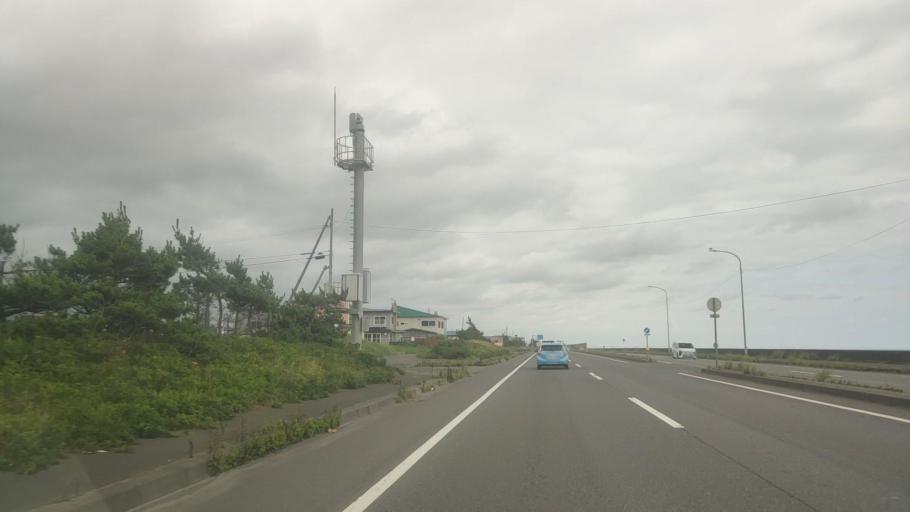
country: JP
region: Hokkaido
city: Shiraoi
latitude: 42.5466
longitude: 141.3581
